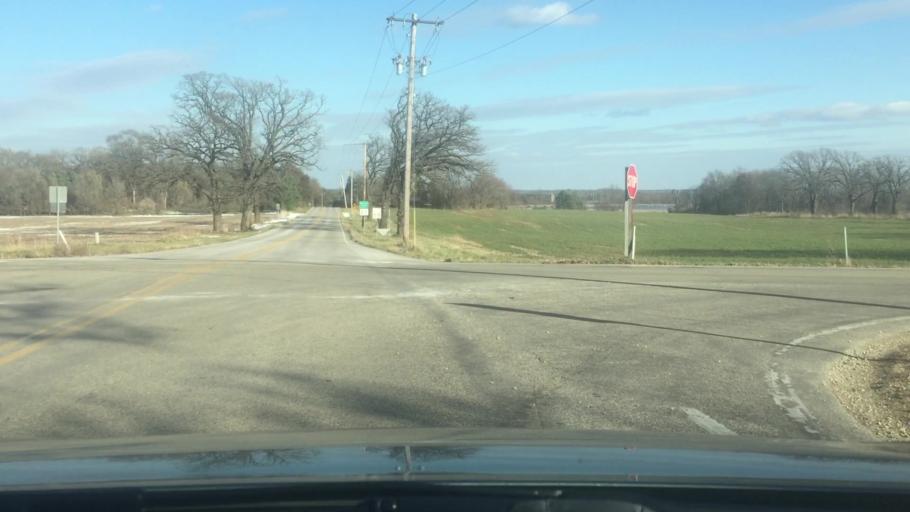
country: US
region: Wisconsin
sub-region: Jefferson County
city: Palmyra
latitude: 42.9270
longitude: -88.5423
